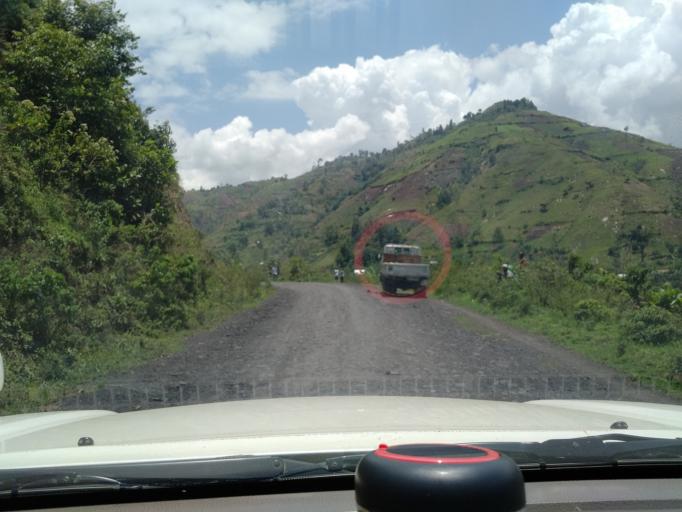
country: CD
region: Nord Kivu
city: Sake
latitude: -1.7442
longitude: 28.9904
